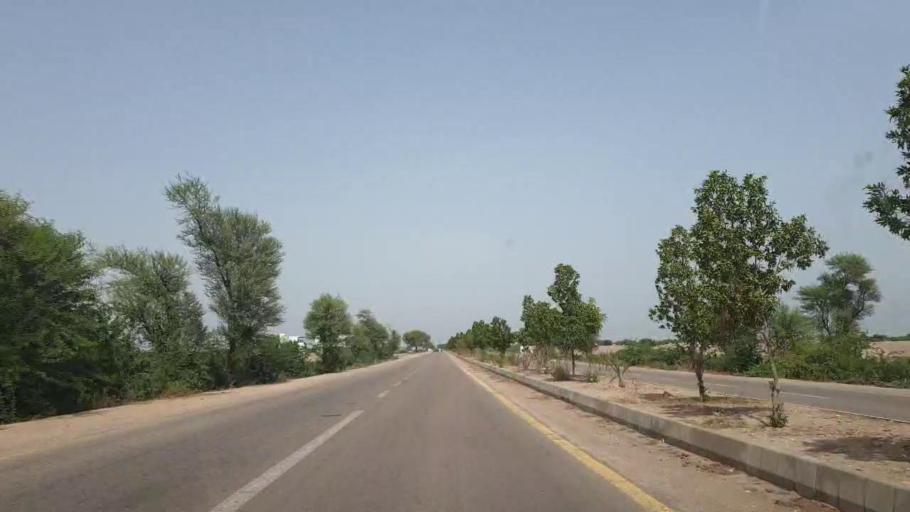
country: PK
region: Sindh
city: Sakrand
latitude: 26.1605
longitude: 68.2603
